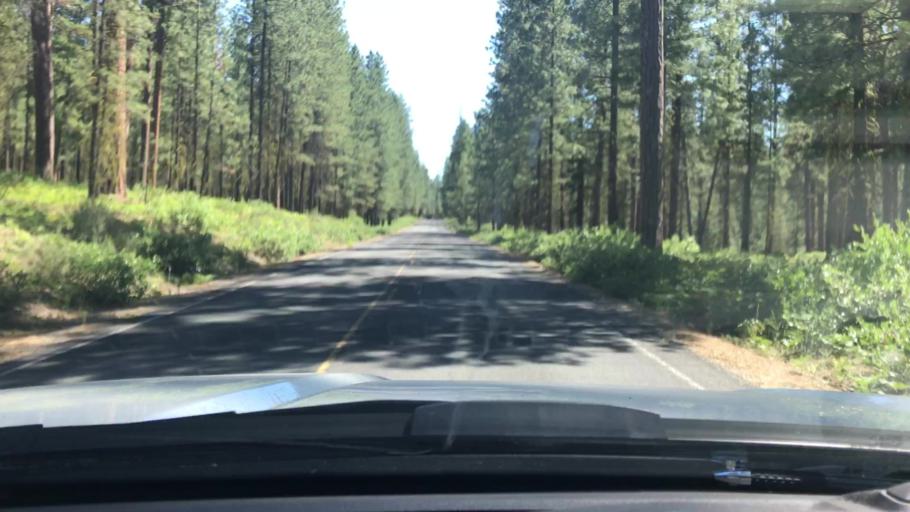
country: US
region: Oregon
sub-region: Deschutes County
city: Sisters
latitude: 44.4084
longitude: -121.6737
